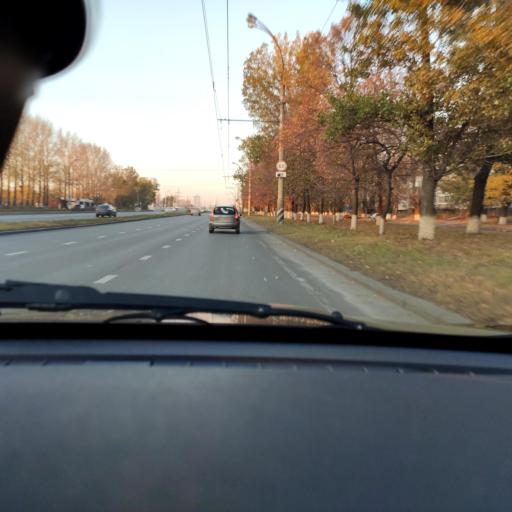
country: RU
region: Samara
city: Tol'yatti
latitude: 53.5265
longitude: 49.2608
